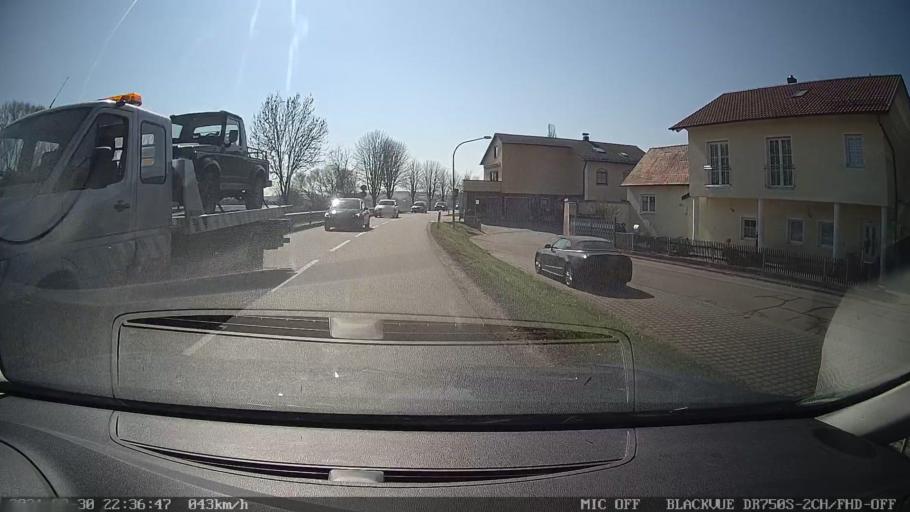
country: DE
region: Bavaria
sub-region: Upper Palatinate
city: Zeitlarn
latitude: 49.0919
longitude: 12.1092
